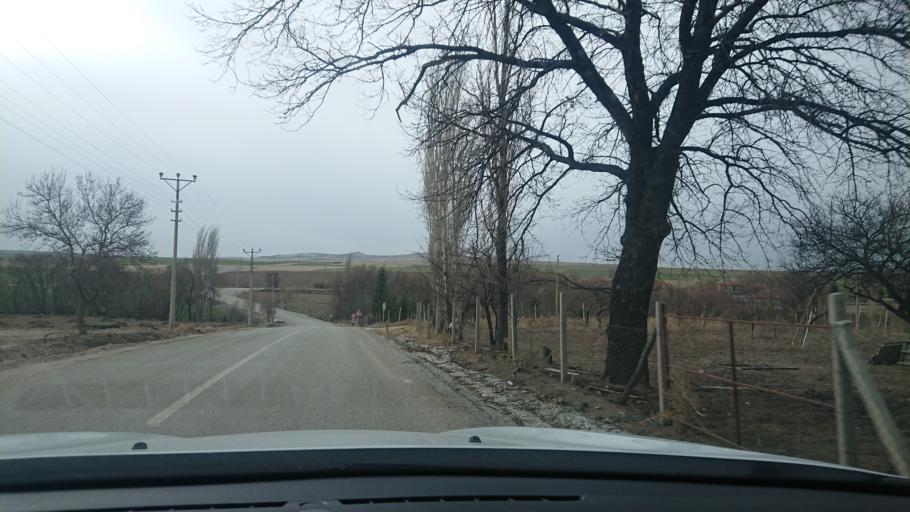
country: TR
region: Aksaray
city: Agacoren
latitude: 38.9256
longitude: 33.9512
